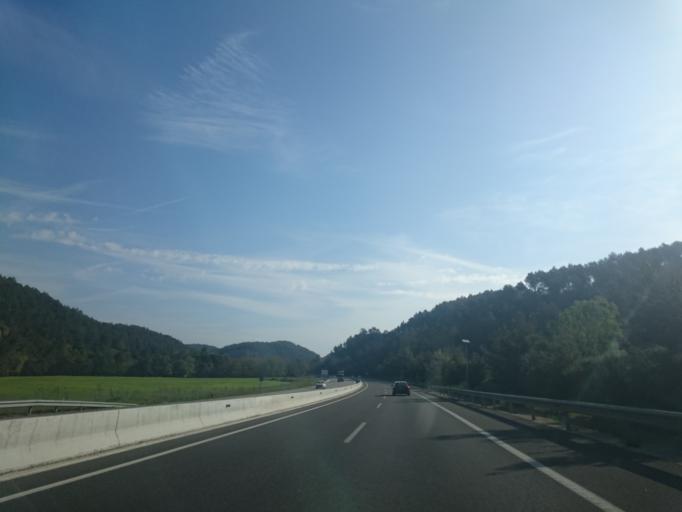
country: ES
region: Catalonia
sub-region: Provincia de Barcelona
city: Avinyo
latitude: 41.8344
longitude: 1.9759
